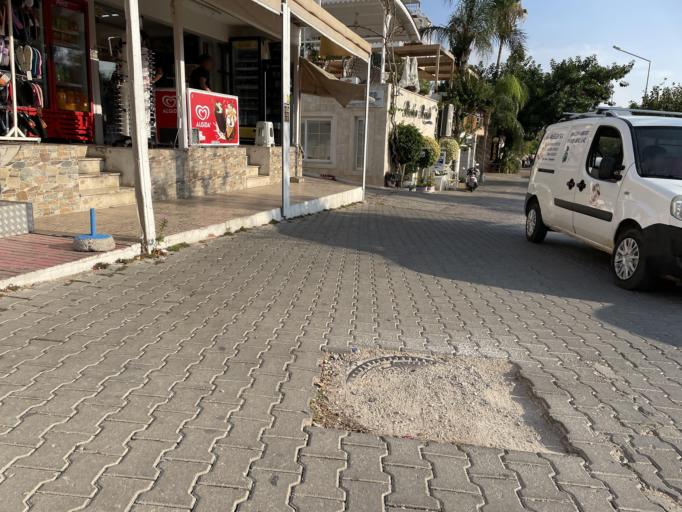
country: TR
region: Antalya
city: Kas
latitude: 36.1980
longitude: 29.6441
